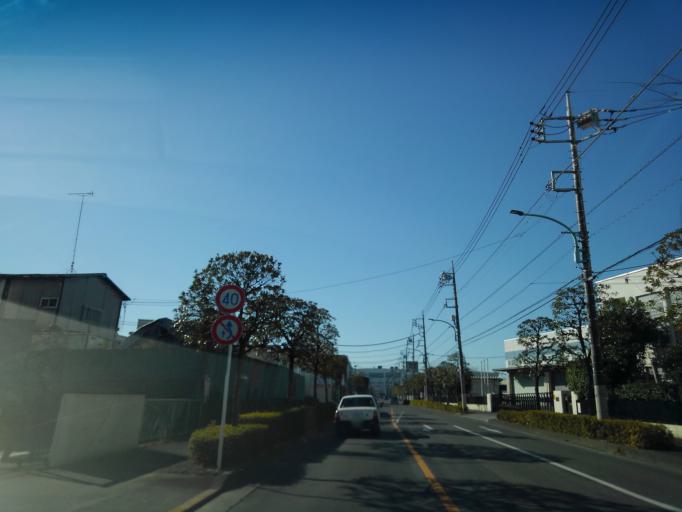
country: JP
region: Tokyo
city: Fussa
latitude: 35.7790
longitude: 139.3225
